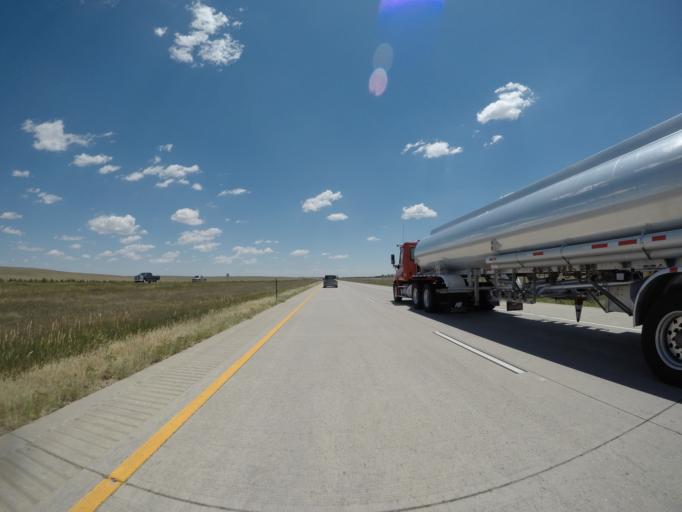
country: US
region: Colorado
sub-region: Lincoln County
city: Limon
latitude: 39.2782
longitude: -103.7578
